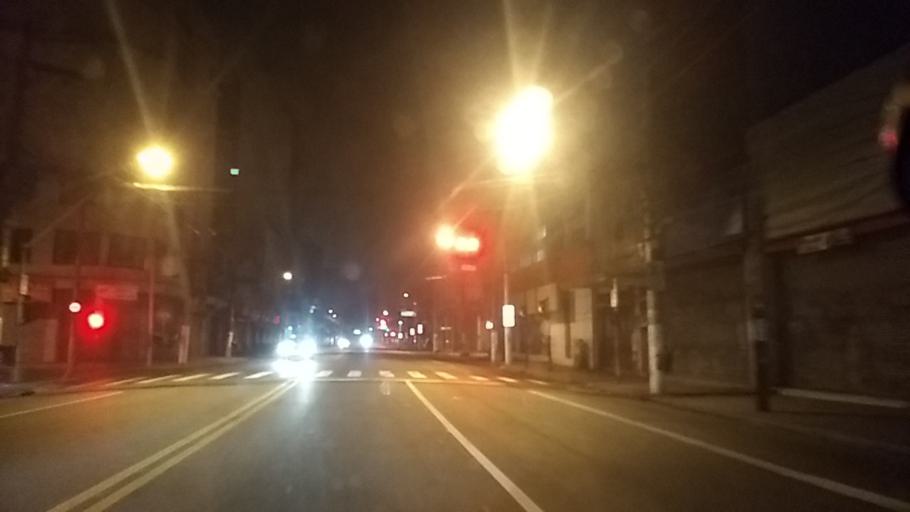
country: BR
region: Sao Paulo
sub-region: Sao Paulo
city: Sao Paulo
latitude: -23.5416
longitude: -46.6144
